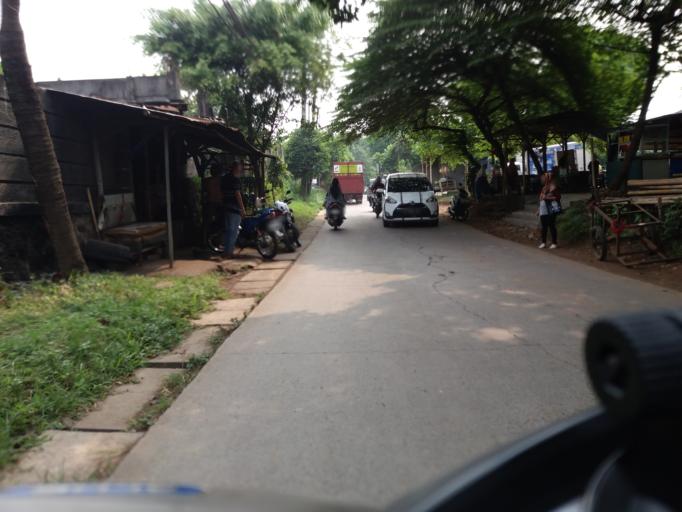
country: ID
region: West Java
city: Cibinong
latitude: -6.4443
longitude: 106.8583
